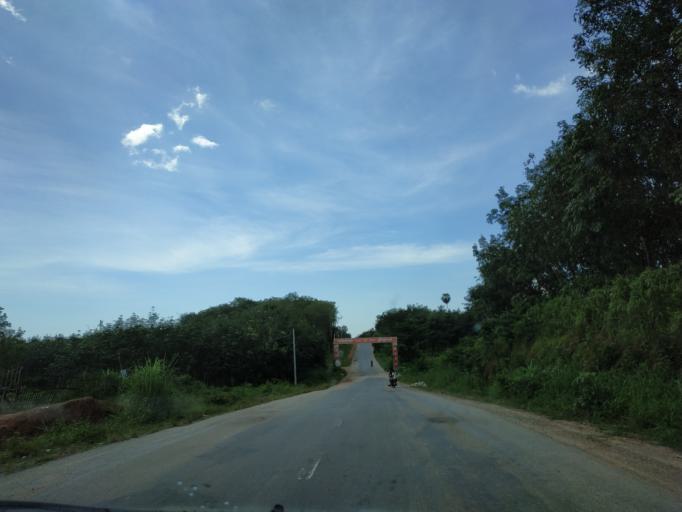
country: MM
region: Mon
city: Kyaikkami
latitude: 15.5047
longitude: 97.8626
